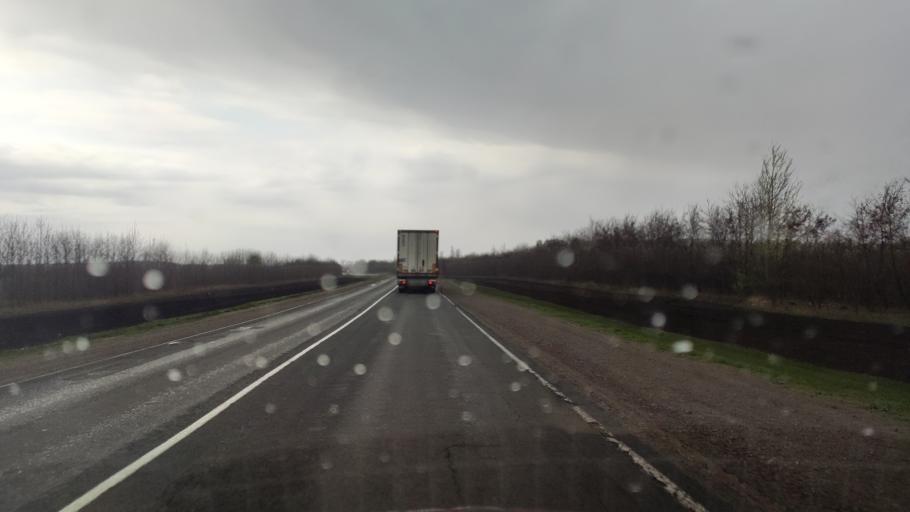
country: RU
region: Voronezj
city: Nizhnedevitsk
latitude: 51.5719
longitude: 38.3321
